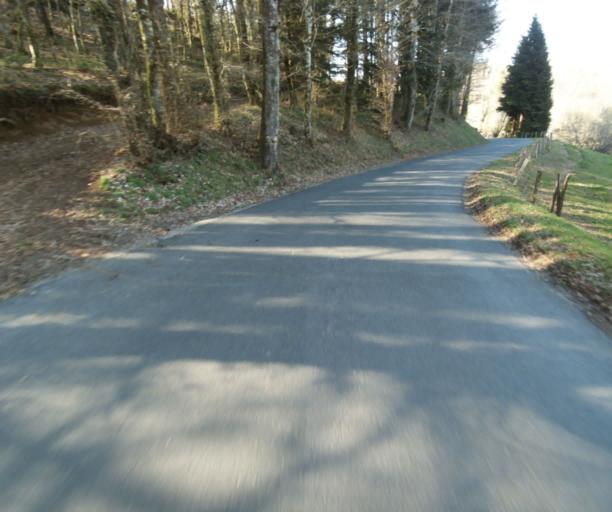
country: FR
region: Limousin
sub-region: Departement de la Correze
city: Tulle
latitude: 45.2874
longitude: 1.7221
